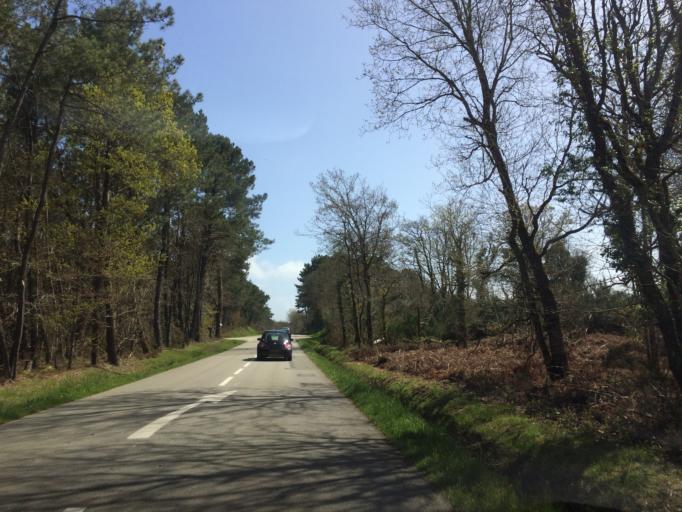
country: FR
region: Brittany
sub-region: Departement du Morbihan
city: La Trinite-sur-Mer
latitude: 47.6092
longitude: -3.0474
